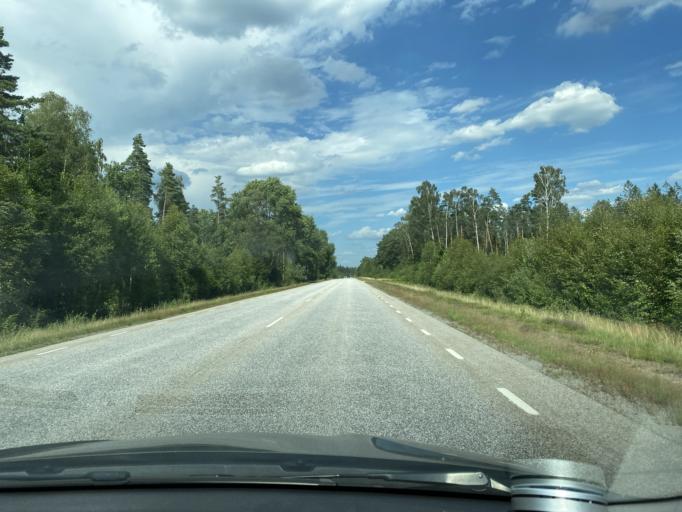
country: SE
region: Kronoberg
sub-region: Markaryds Kommun
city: Markaryd
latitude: 56.4169
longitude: 13.5446
